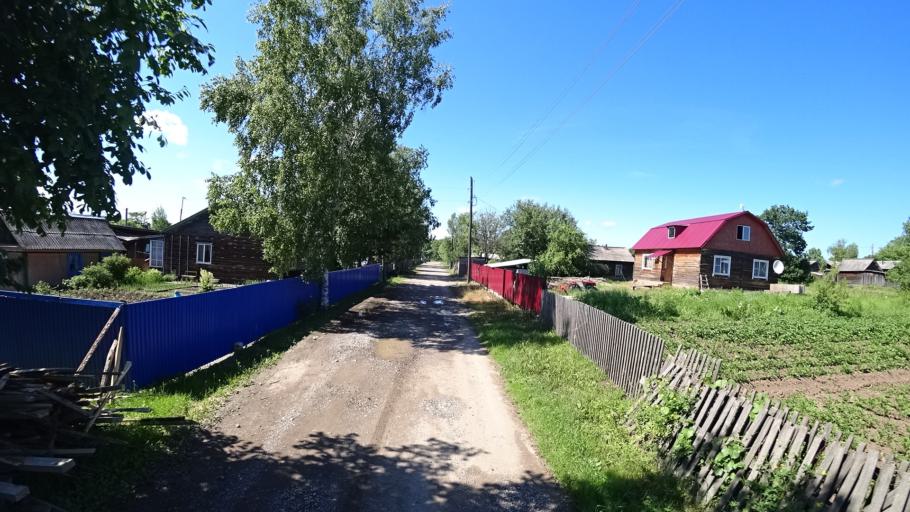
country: RU
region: Khabarovsk Krai
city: Khor
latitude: 47.8877
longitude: 135.0255
